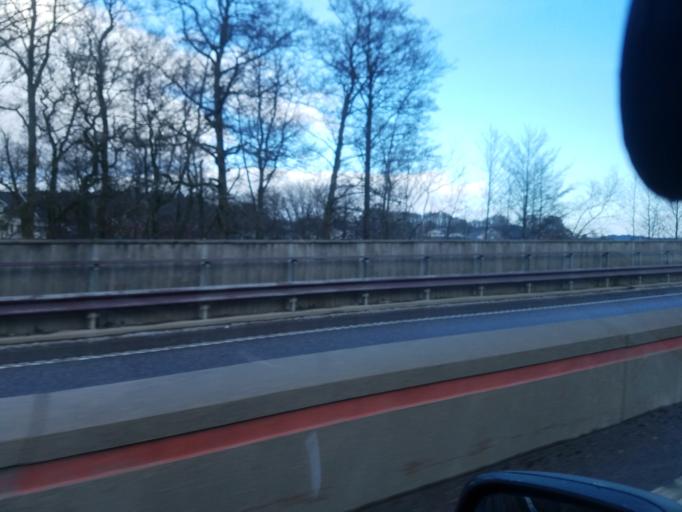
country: SE
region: Vaestra Goetaland
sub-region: Orust
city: Henan
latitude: 58.3487
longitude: 11.7475
